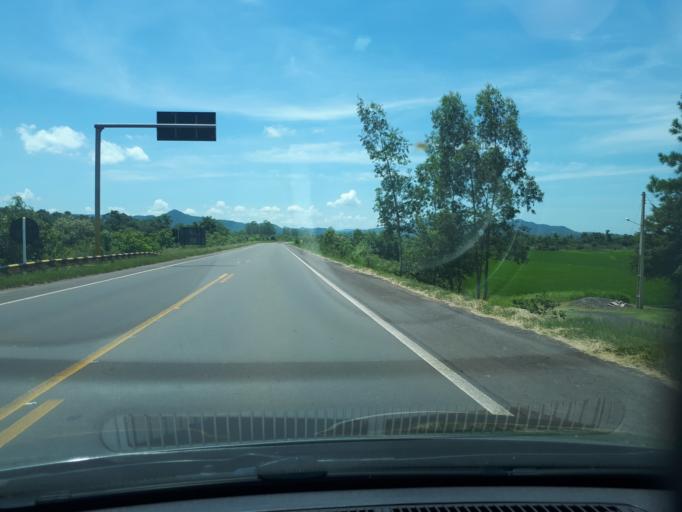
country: BR
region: Rio Grande do Sul
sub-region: Candelaria
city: Candelaria
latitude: -29.7309
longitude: -52.9442
